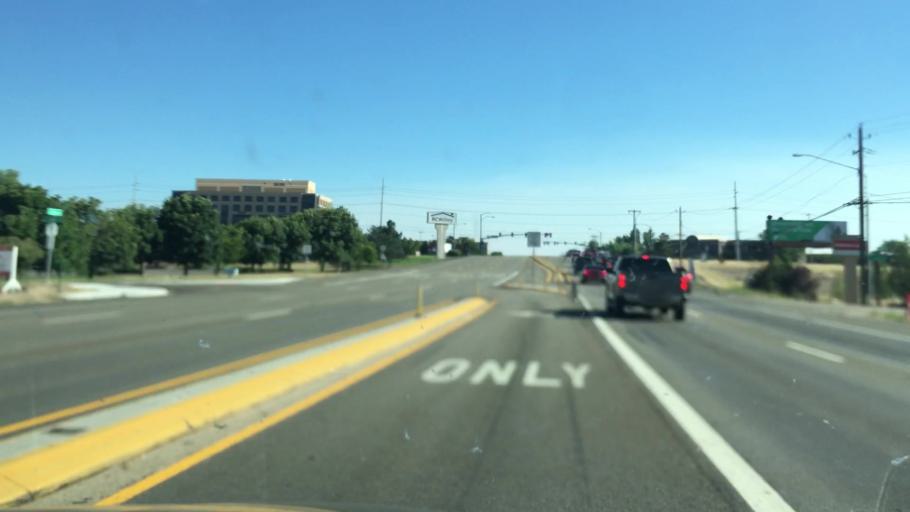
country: US
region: Idaho
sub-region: Ada County
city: Meridian
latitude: 43.6076
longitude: -116.3548
